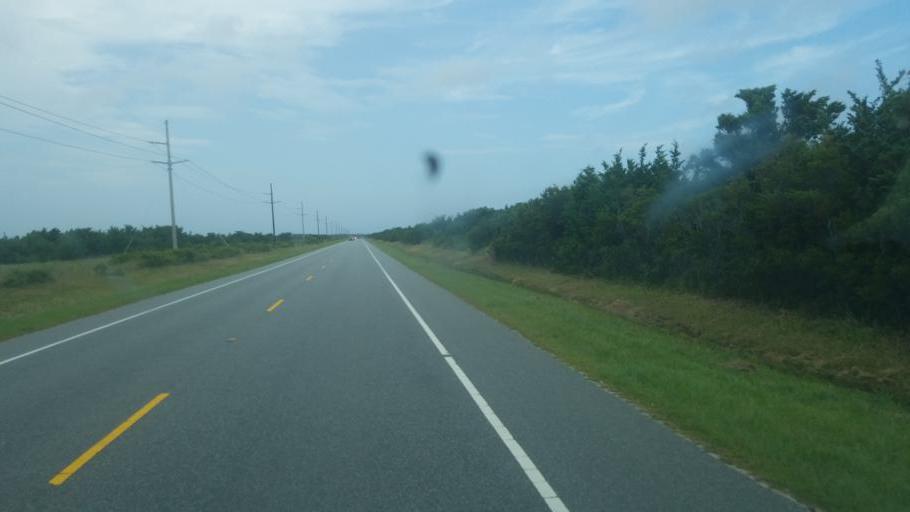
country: US
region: North Carolina
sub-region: Dare County
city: Buxton
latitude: 35.4889
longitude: -75.4810
